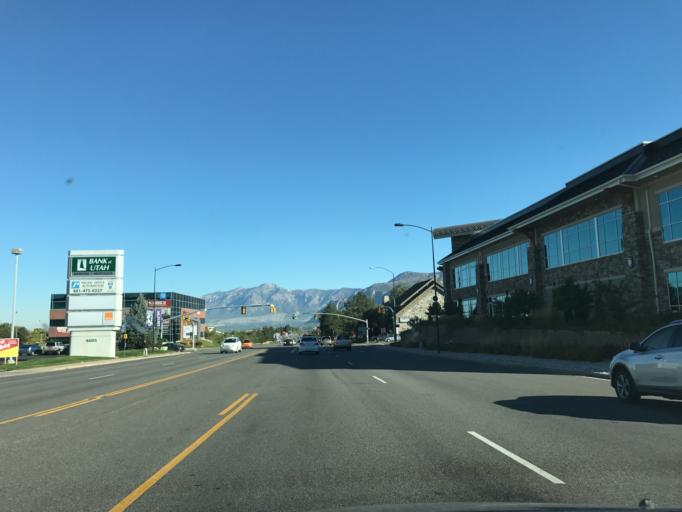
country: US
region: Utah
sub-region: Weber County
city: South Ogden
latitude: 41.1787
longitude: -111.9492
